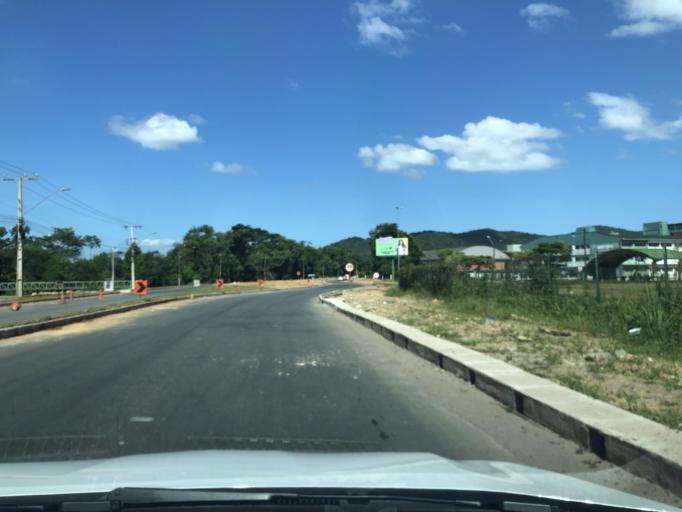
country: BR
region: Santa Catarina
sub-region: Joinville
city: Joinville
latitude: -26.2497
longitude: -48.8581
